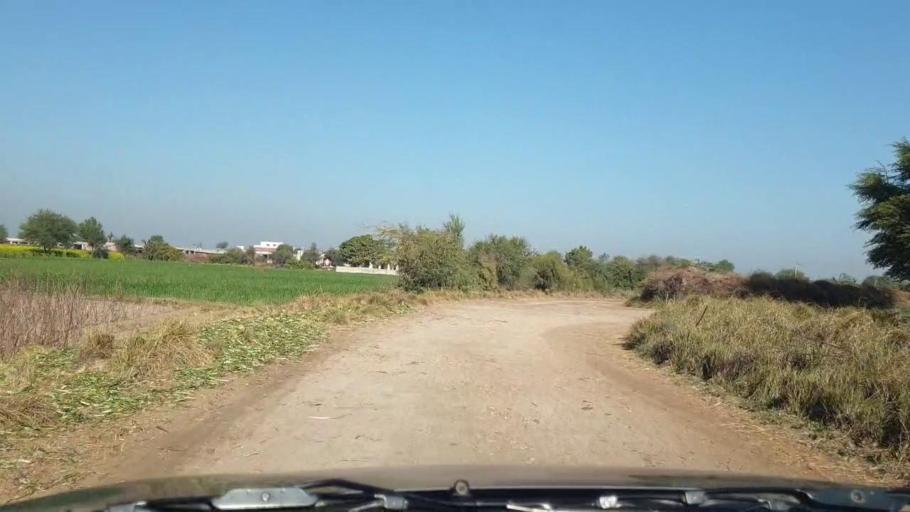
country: PK
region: Sindh
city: Jhol
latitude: 25.9456
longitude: 68.8219
